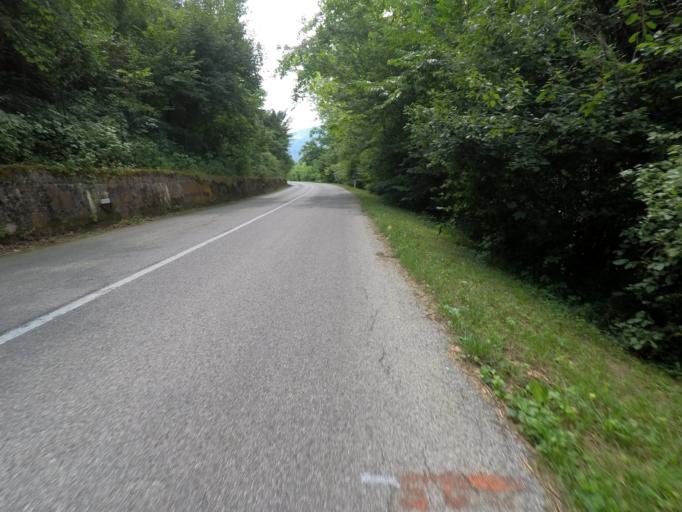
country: IT
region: Friuli Venezia Giulia
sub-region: Provincia di Pordenone
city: Polcenigo
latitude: 46.0241
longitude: 12.4892
